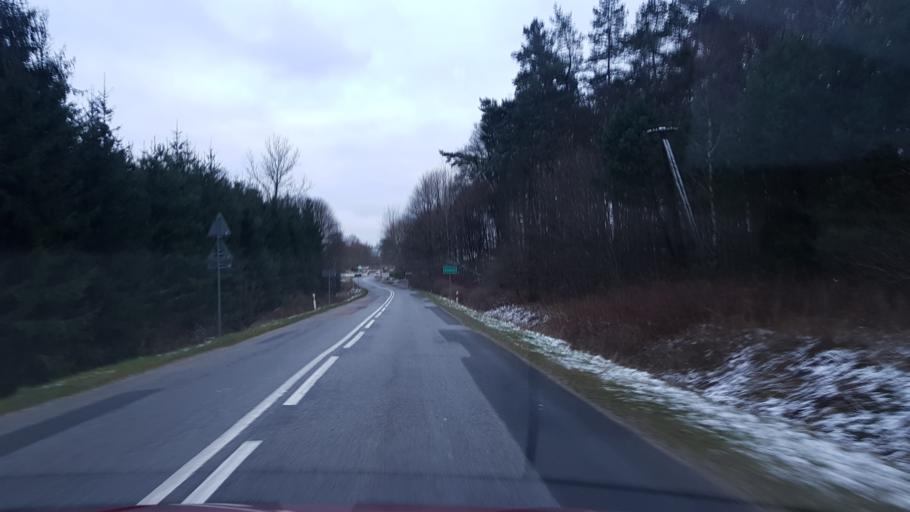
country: PL
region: Pomeranian Voivodeship
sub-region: Powiat bytowski
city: Miastko
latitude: 54.0247
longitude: 16.9478
